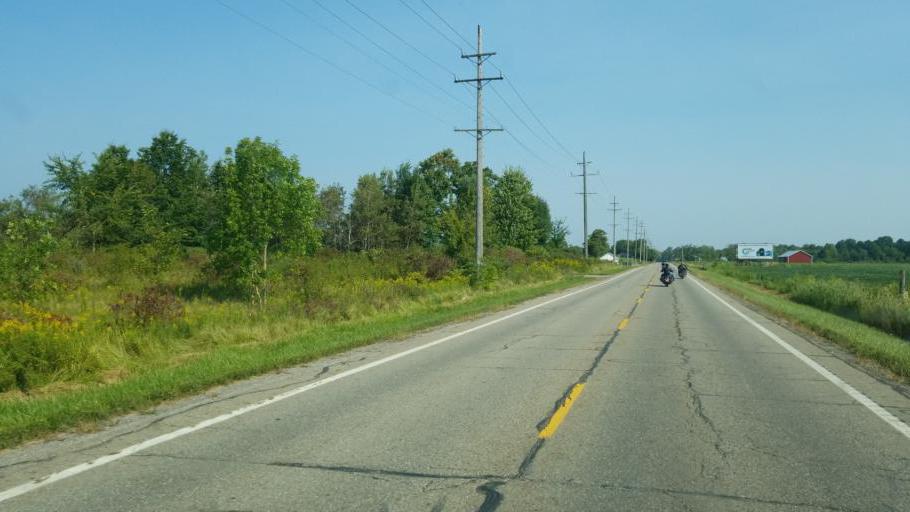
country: US
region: Ohio
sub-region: Ashtabula County
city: Orwell
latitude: 41.5634
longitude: -80.8658
